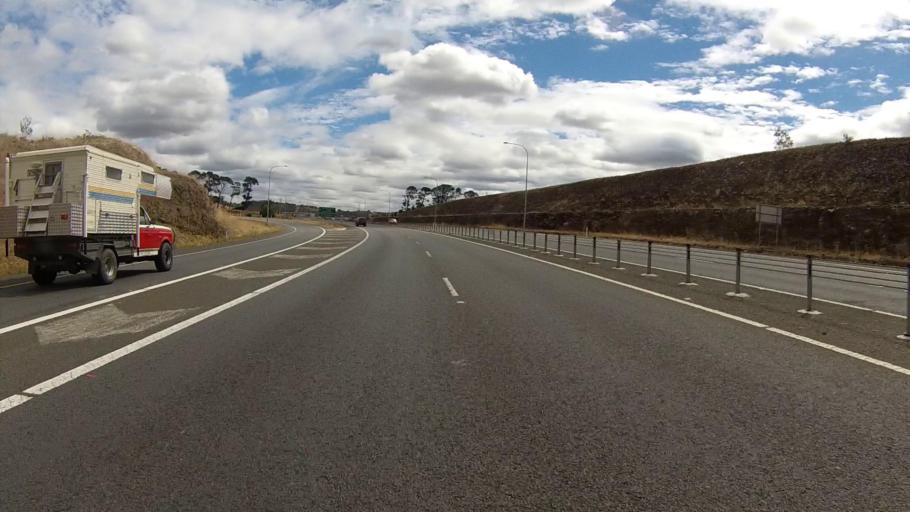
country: AU
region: Tasmania
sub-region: Brighton
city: Bridgewater
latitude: -42.7309
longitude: 147.2378
